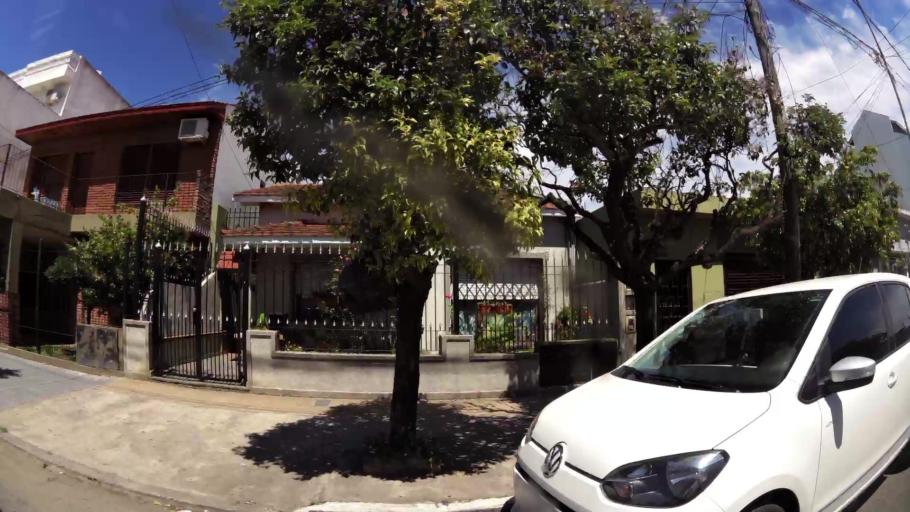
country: AR
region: Buenos Aires
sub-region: Partido de Quilmes
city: Quilmes
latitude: -34.7309
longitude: -58.3040
